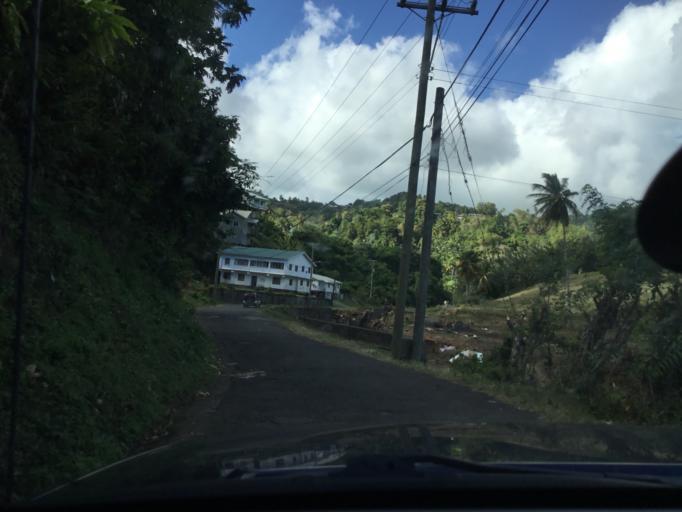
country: VC
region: Saint George
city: Kingstown
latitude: 13.1453
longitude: -61.1745
